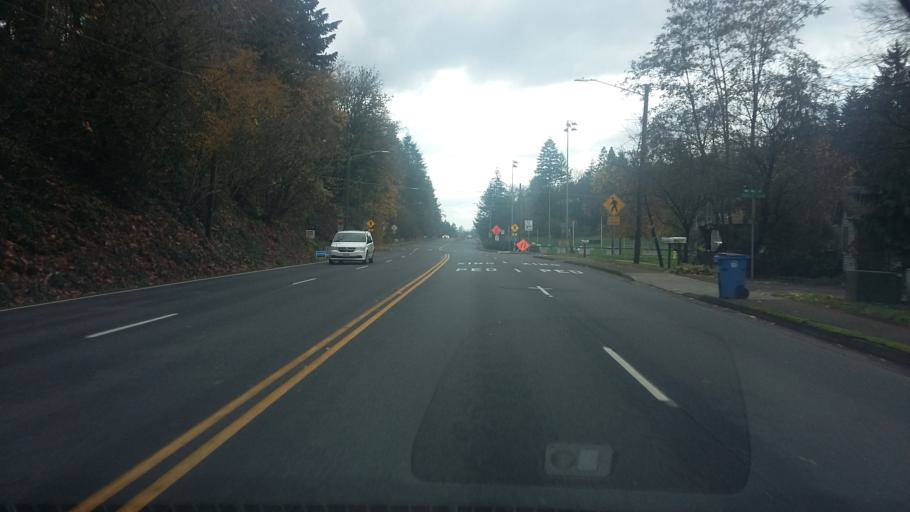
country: US
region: Washington
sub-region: Clark County
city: Camas
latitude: 45.5839
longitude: -122.4191
